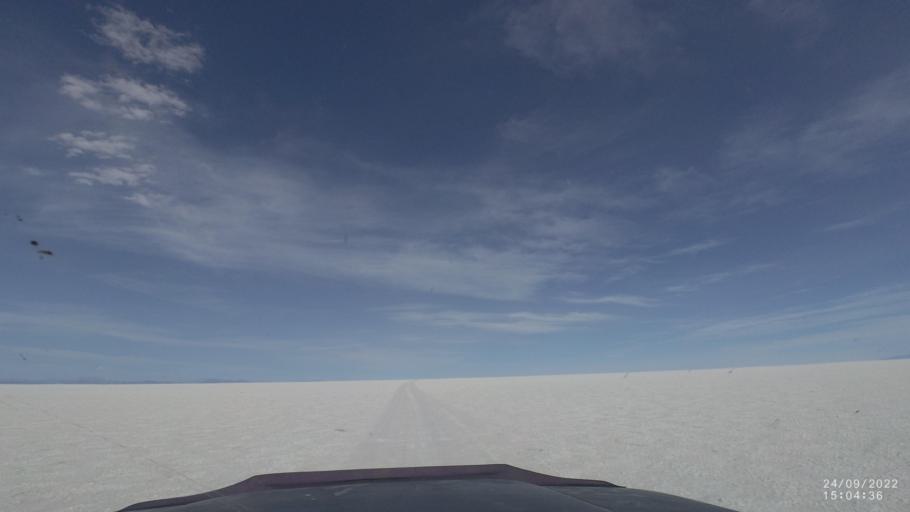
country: BO
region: Potosi
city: Colchani
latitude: -19.9008
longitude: -67.5233
